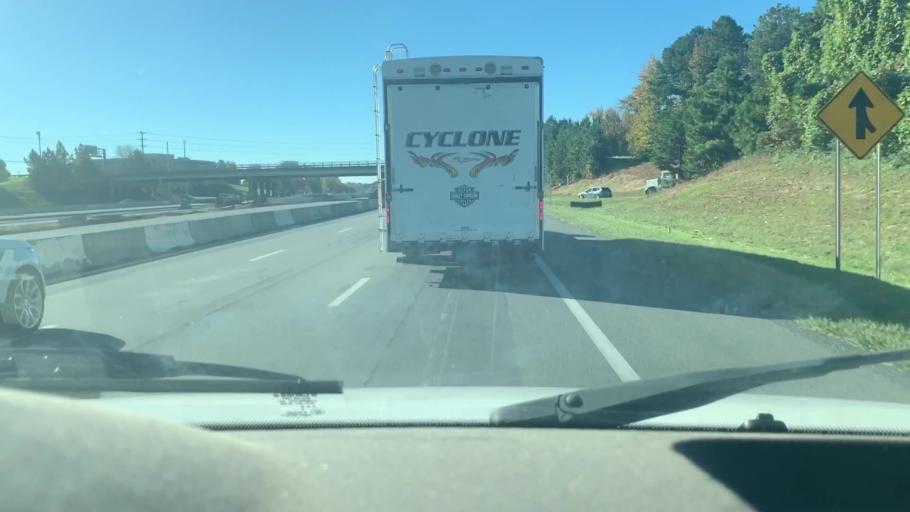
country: US
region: North Carolina
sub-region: Mecklenburg County
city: Huntersville
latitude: 35.3499
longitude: -80.8475
